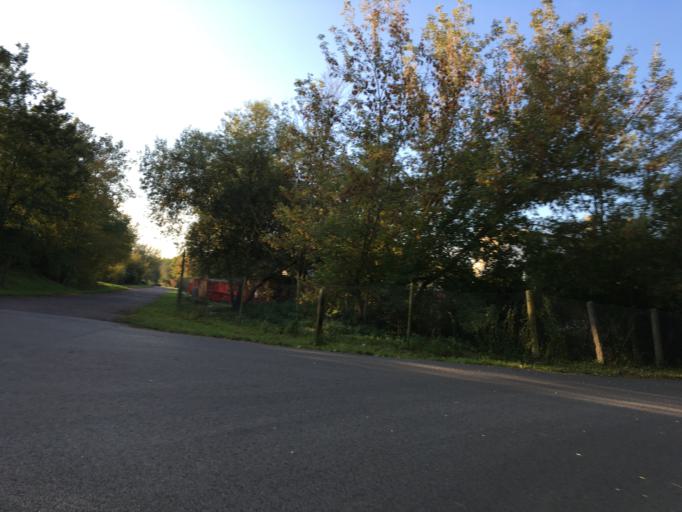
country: DE
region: Brandenburg
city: Frankfurt (Oder)
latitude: 52.3652
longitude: 14.5452
